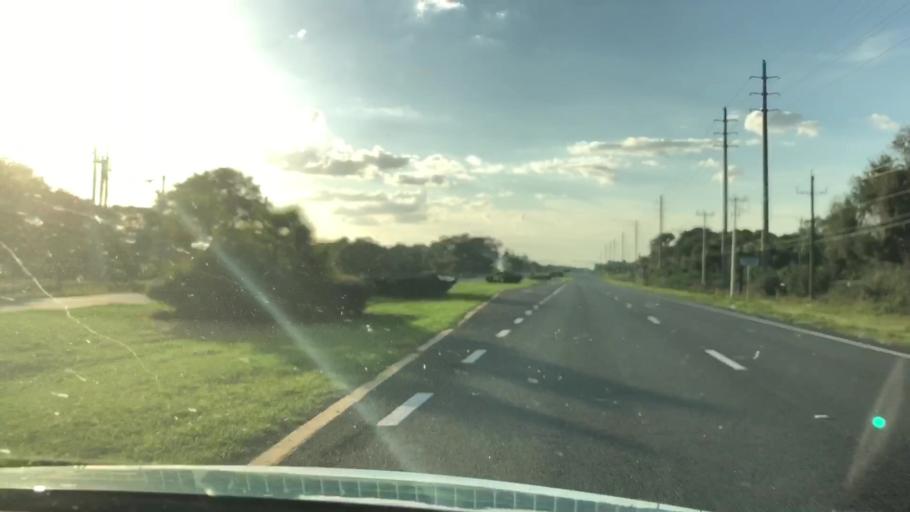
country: US
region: Florida
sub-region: Brevard County
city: Port Saint John
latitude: 28.5291
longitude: -80.8055
